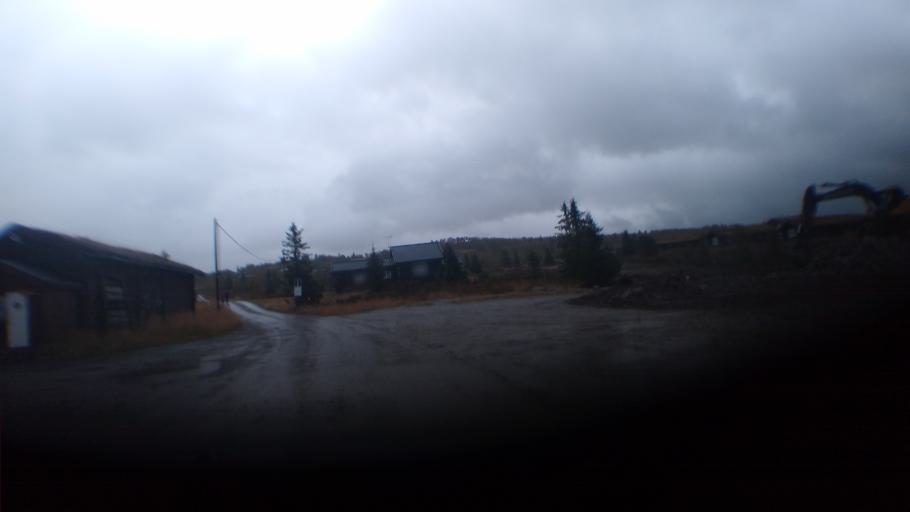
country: NO
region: Oppland
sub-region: Ringebu
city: Ringebu
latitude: 61.6483
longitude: 10.0947
